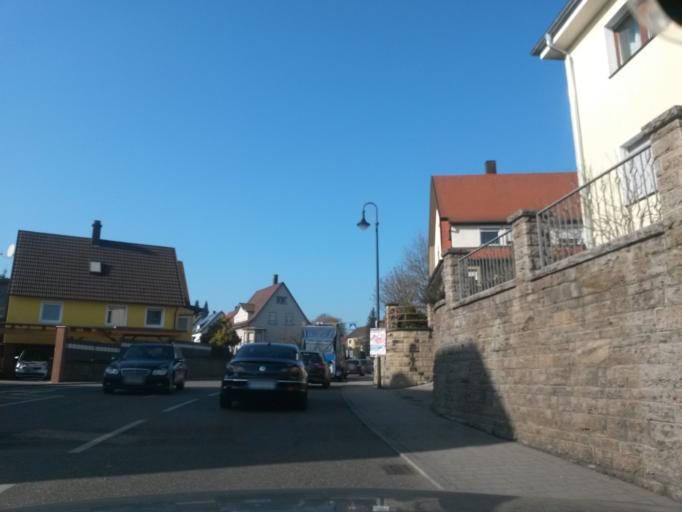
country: DE
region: Baden-Wuerttemberg
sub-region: Karlsruhe Region
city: Muhlacker
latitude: 48.9484
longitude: 8.8362
